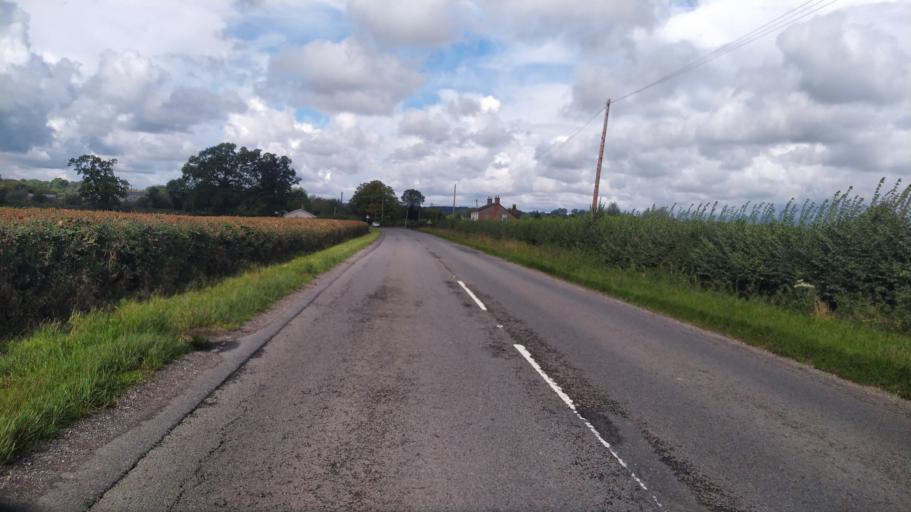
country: GB
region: England
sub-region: Dorset
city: Sturminster Newton
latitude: 50.9211
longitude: -2.3471
